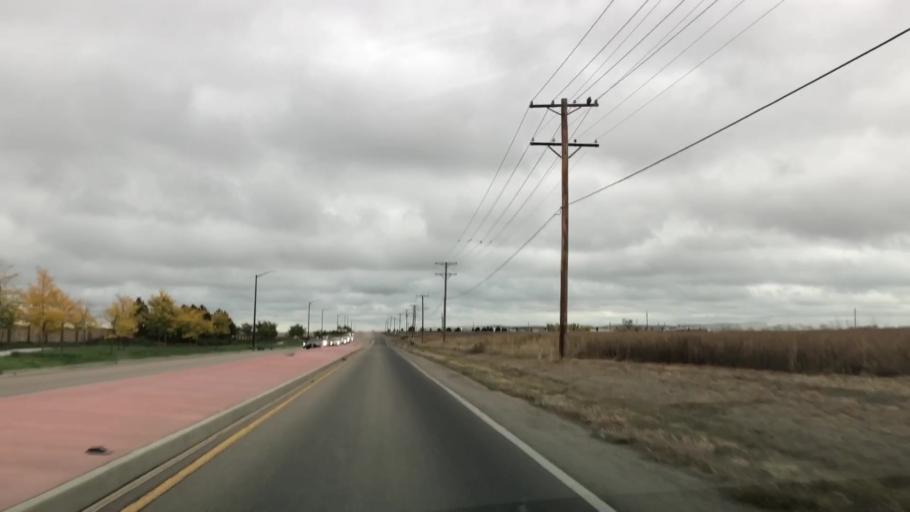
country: US
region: Colorado
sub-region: Larimer County
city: Loveland
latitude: 40.4349
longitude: -105.0211
